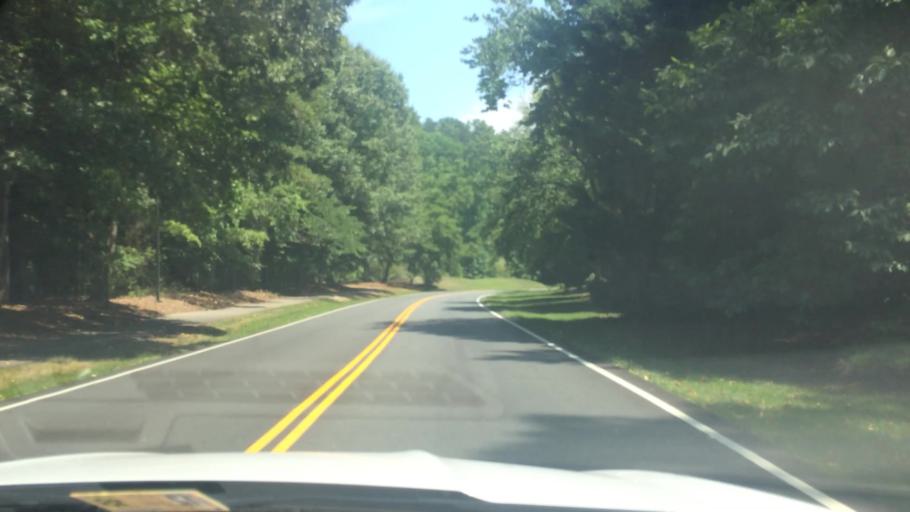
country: US
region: Virginia
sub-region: City of Williamsburg
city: Williamsburg
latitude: 37.2299
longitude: -76.6499
